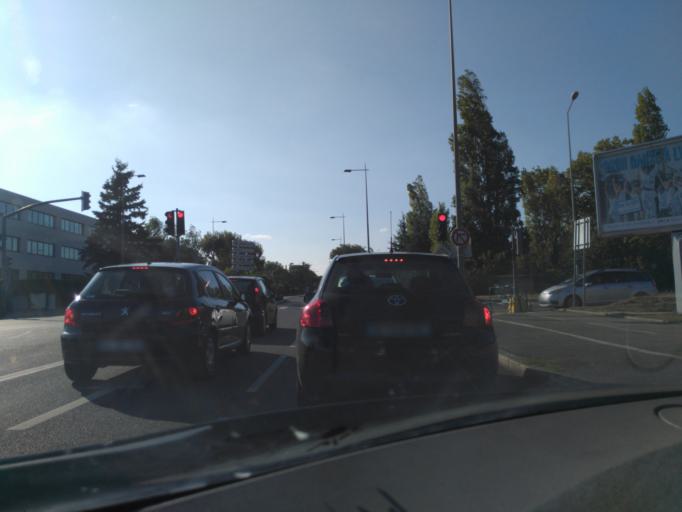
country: FR
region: Rhone-Alpes
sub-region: Departement du Rhone
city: Bron
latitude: 45.7273
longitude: 4.9277
